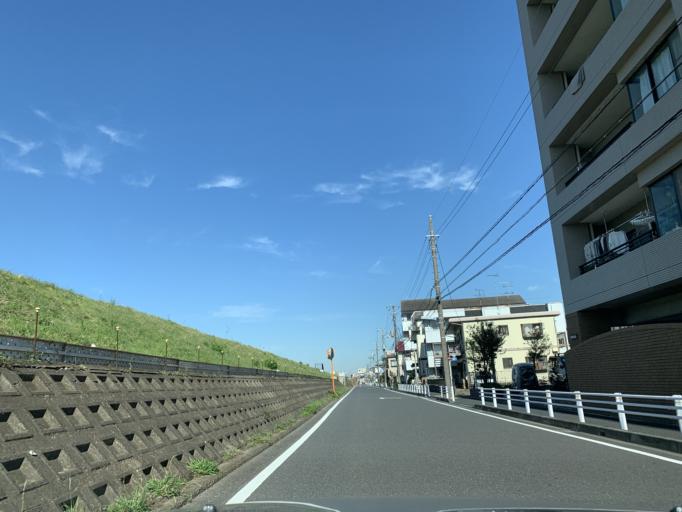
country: JP
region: Tokyo
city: Urayasu
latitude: 35.6499
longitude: 139.8866
